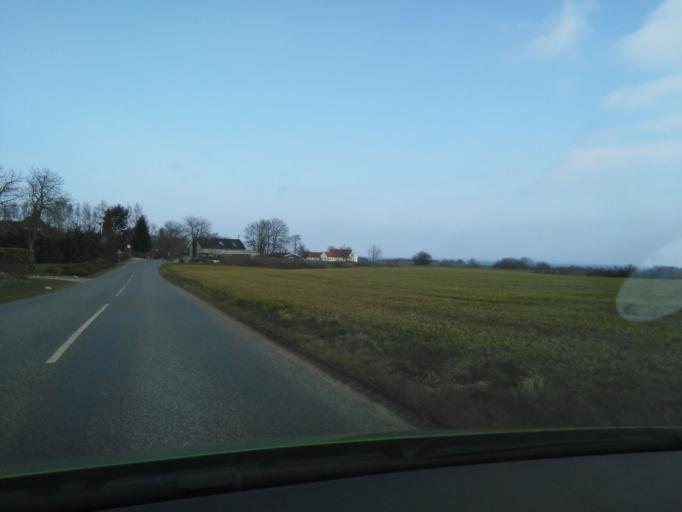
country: DK
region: Central Jutland
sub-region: Arhus Kommune
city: Beder
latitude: 56.0448
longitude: 10.2395
